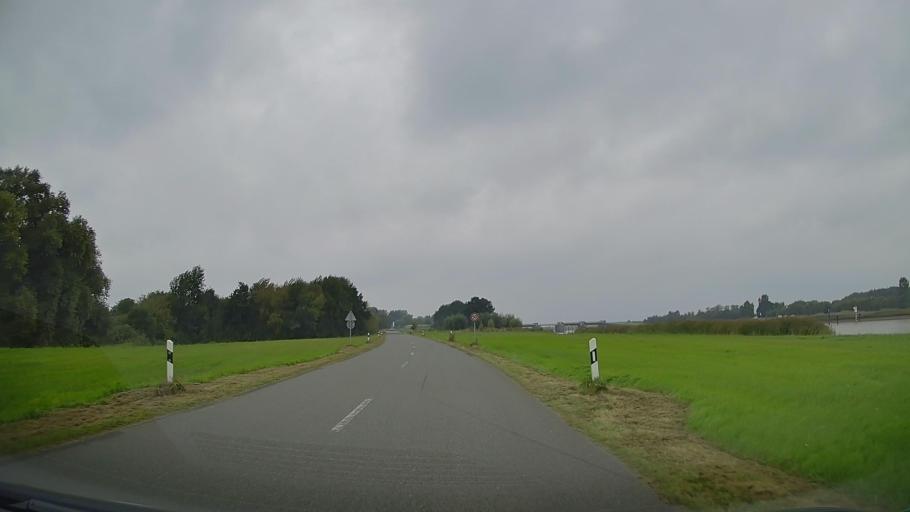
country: DE
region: Lower Saxony
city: Neuhaus an der Oste
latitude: 53.8143
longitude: 9.0424
